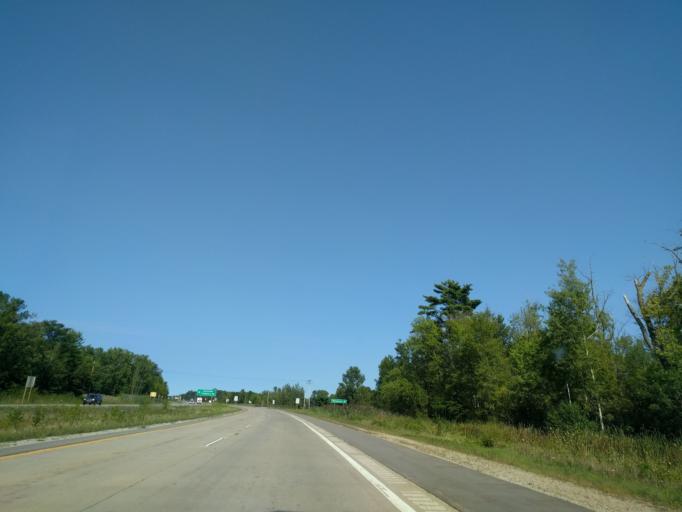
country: US
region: Wisconsin
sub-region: Oconto County
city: Oconto
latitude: 44.8151
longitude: -87.9475
